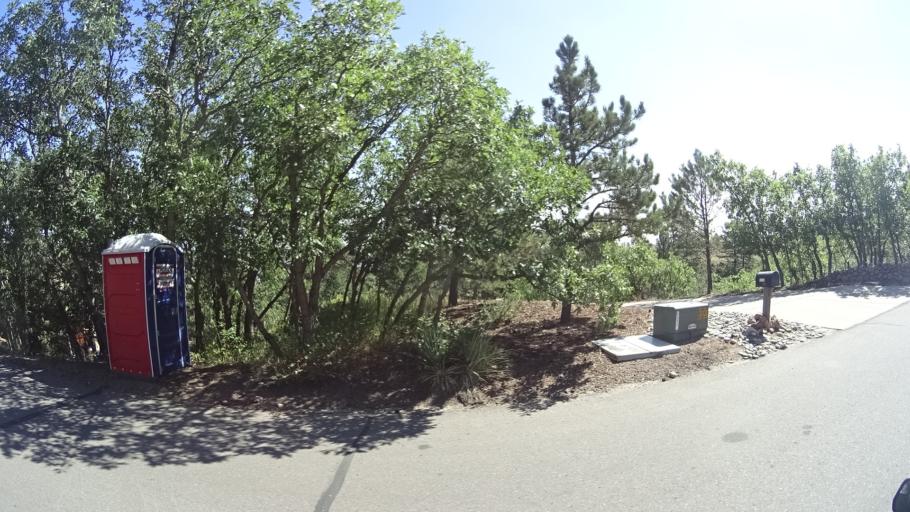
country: US
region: Colorado
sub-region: El Paso County
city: Manitou Springs
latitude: 38.8145
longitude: -104.8807
